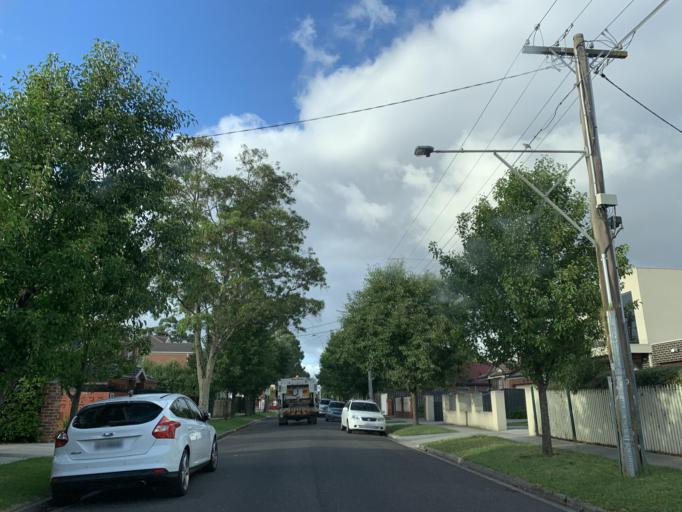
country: AU
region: Victoria
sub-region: Moonee Valley
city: Niddrie
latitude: -37.7385
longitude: 144.8981
